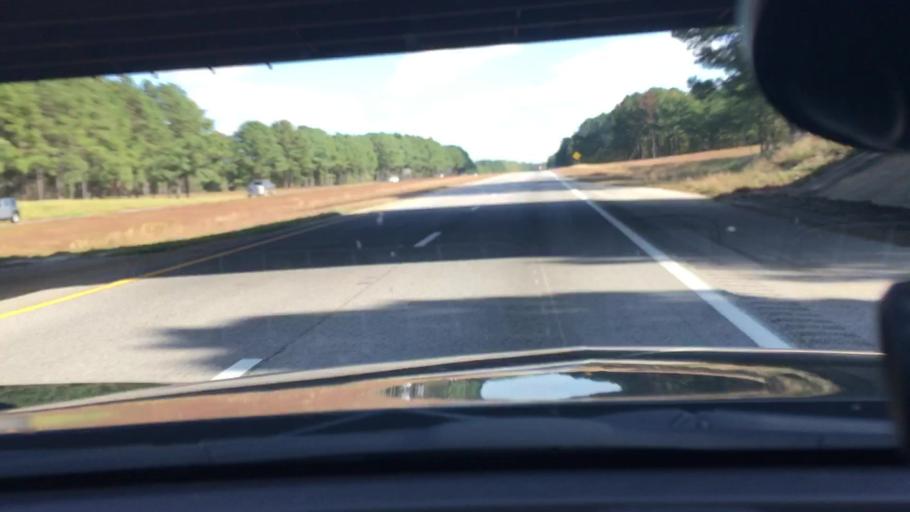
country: US
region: North Carolina
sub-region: Wilson County
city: Lucama
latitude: 35.7740
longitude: -78.0576
